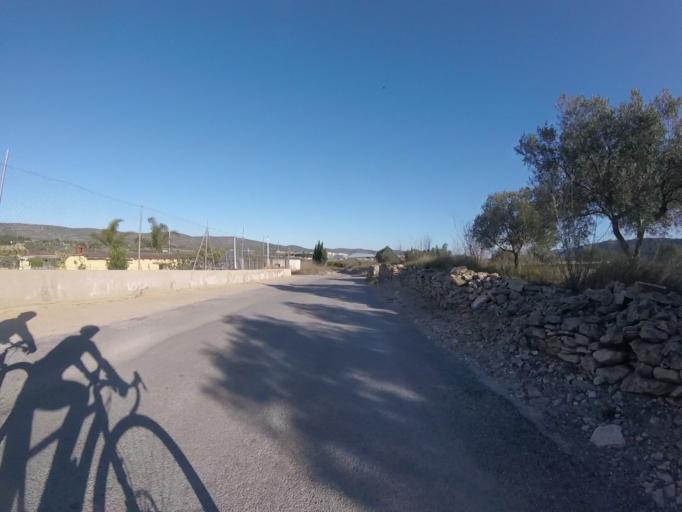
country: ES
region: Valencia
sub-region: Provincia de Castello
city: Alcala de Xivert
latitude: 40.2949
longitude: 0.2191
